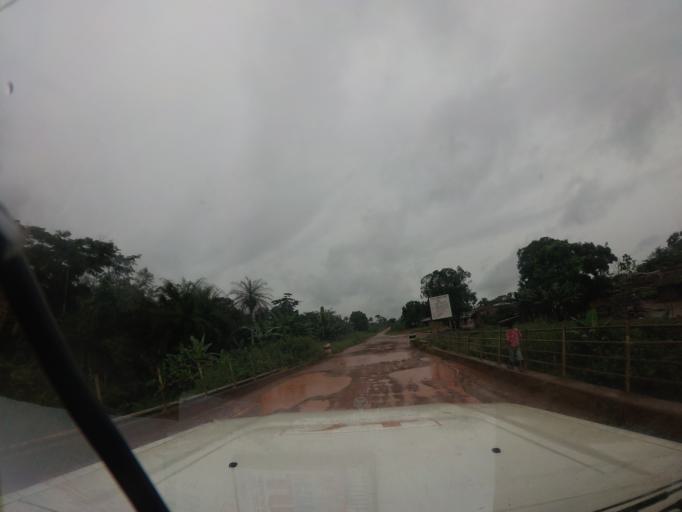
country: SL
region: Eastern Province
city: Tefeya
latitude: 8.5727
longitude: -11.3072
